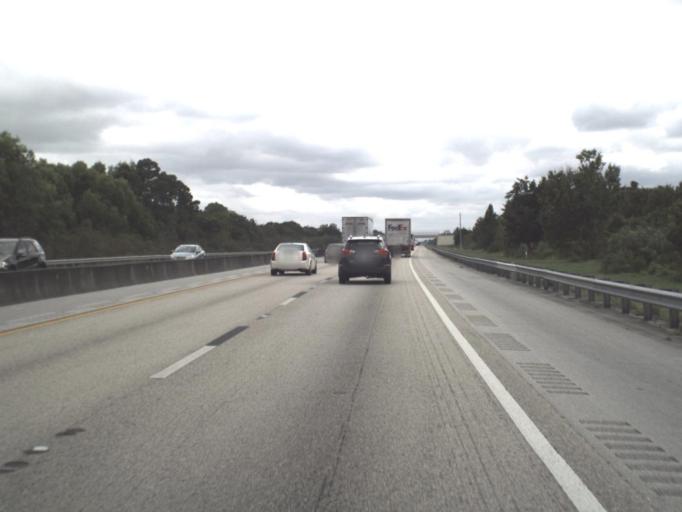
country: US
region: Florida
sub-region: Palm Beach County
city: Palm Beach Gardens
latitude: 26.8718
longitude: -80.1289
